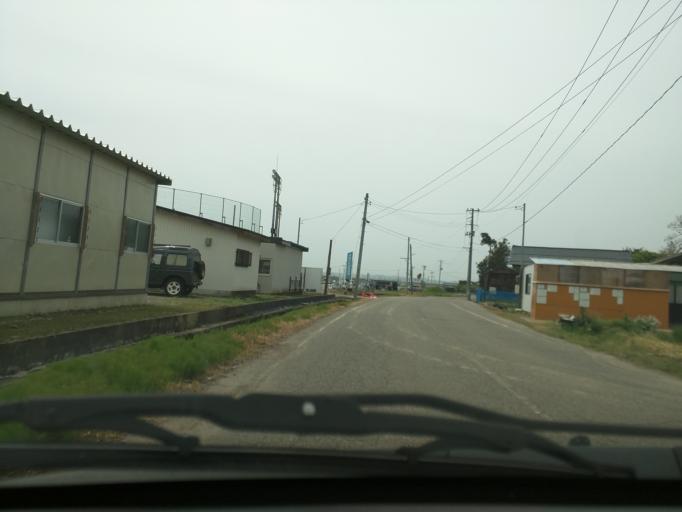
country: JP
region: Niigata
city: Mitsuke
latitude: 37.5512
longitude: 138.9100
